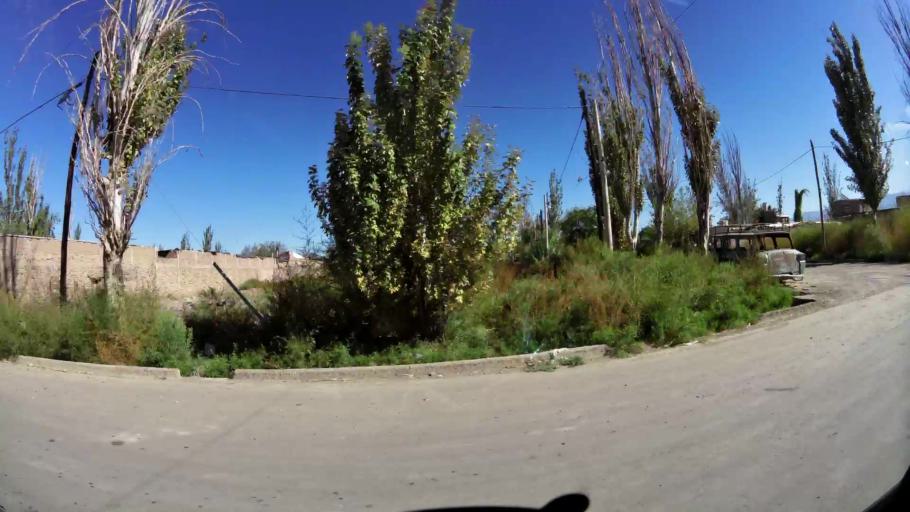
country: AR
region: Mendoza
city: Las Heras
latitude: -32.8364
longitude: -68.8085
